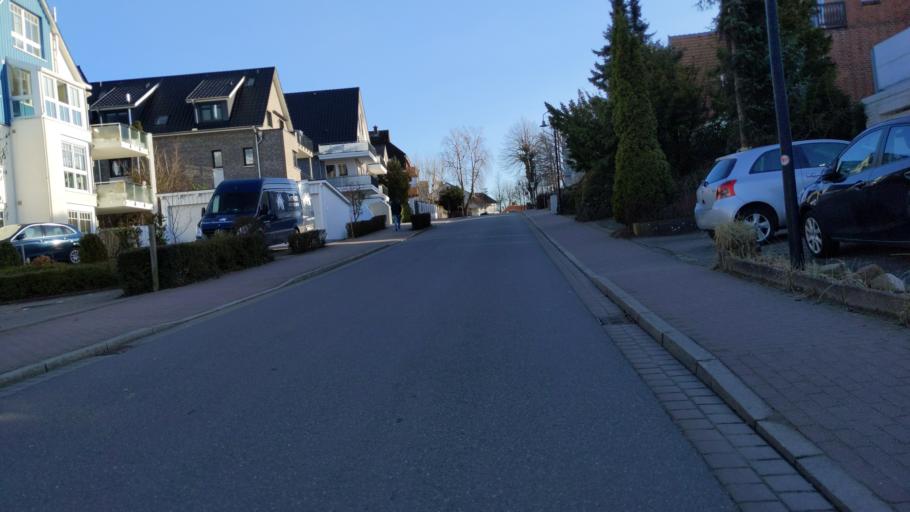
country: DE
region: Schleswig-Holstein
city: Scharbeutz
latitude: 54.0256
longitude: 10.7519
